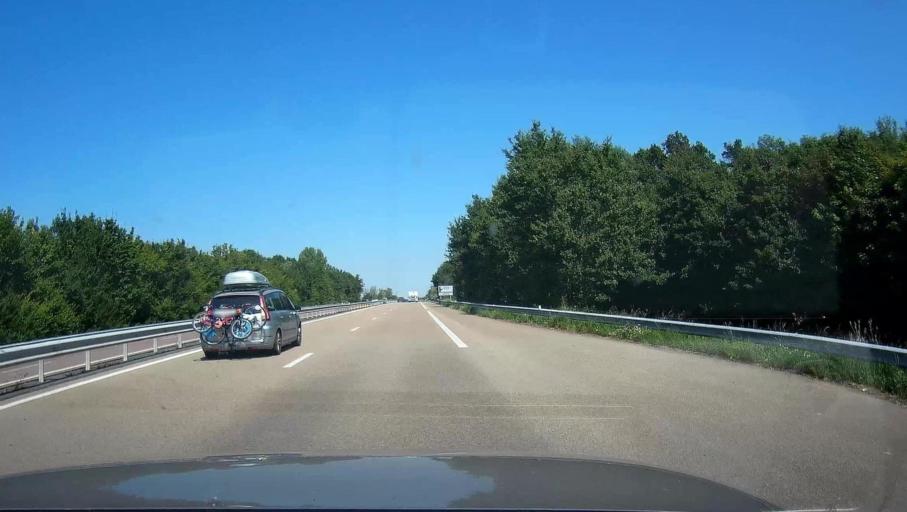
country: FR
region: Champagne-Ardenne
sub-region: Departement de l'Aube
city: Verrieres
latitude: 48.2687
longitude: 4.1645
